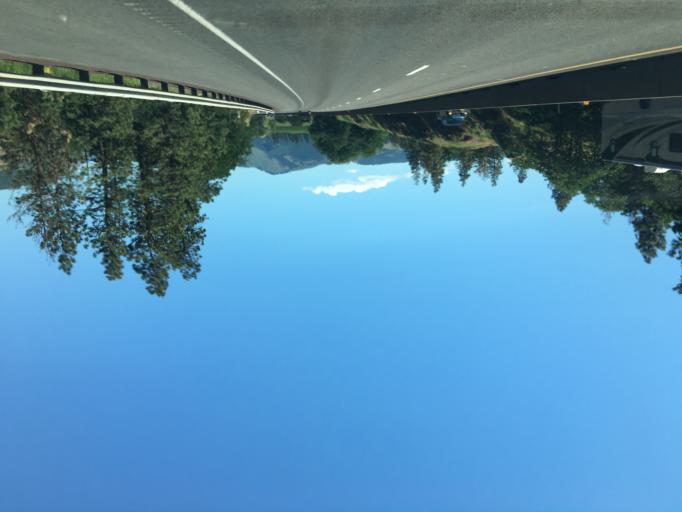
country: US
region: Washington
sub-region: Klickitat County
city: White Salmon
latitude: 45.6948
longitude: -121.3626
